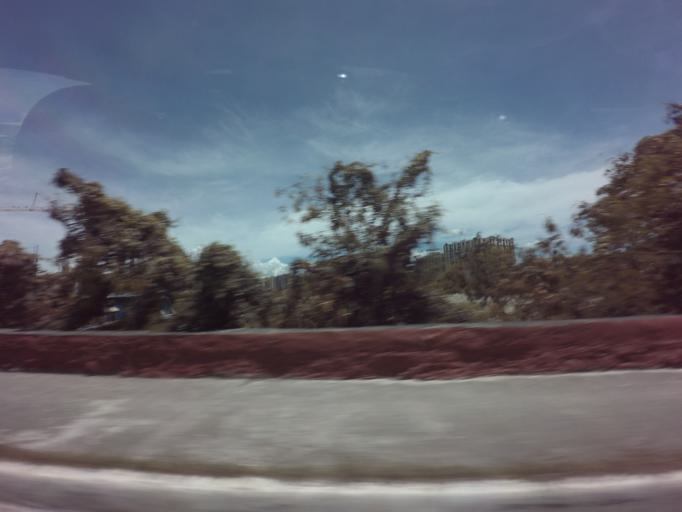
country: PH
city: Sambayanihan People's Village
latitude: 14.4901
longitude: 120.9988
